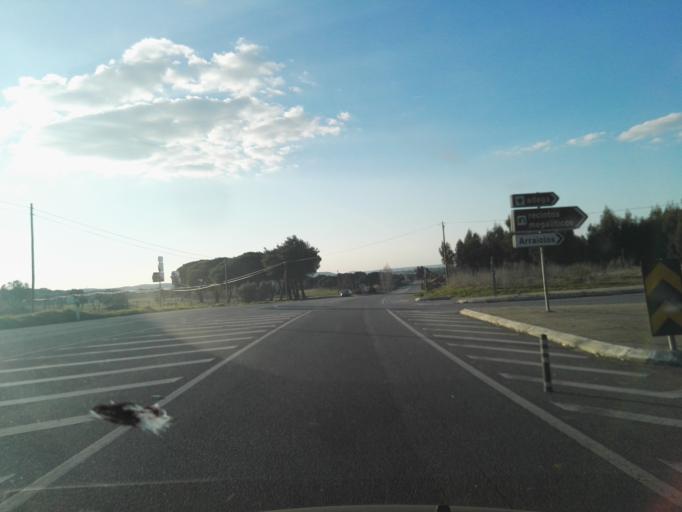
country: PT
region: Evora
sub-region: Arraiolos
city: Arraiolos
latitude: 38.6041
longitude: -8.0514
